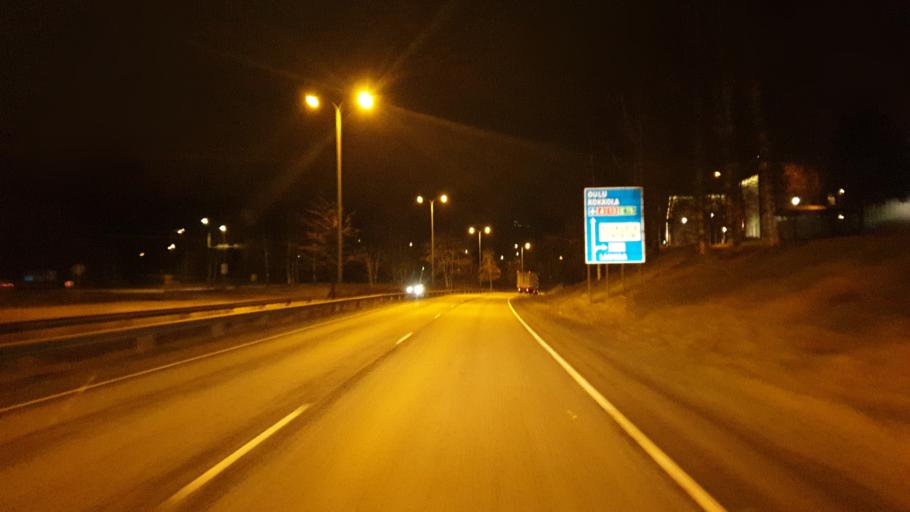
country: FI
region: Central Finland
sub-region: Jyvaeskylae
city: Jyvaeskylae
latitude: 62.2557
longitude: 25.7612
